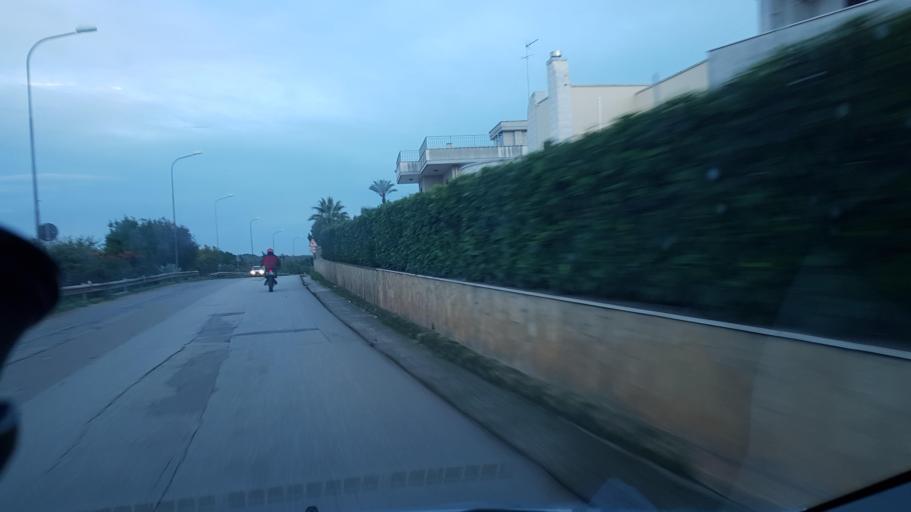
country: IT
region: Apulia
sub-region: Provincia di Brindisi
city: Ceglie Messapica
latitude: 40.6507
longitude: 17.5154
